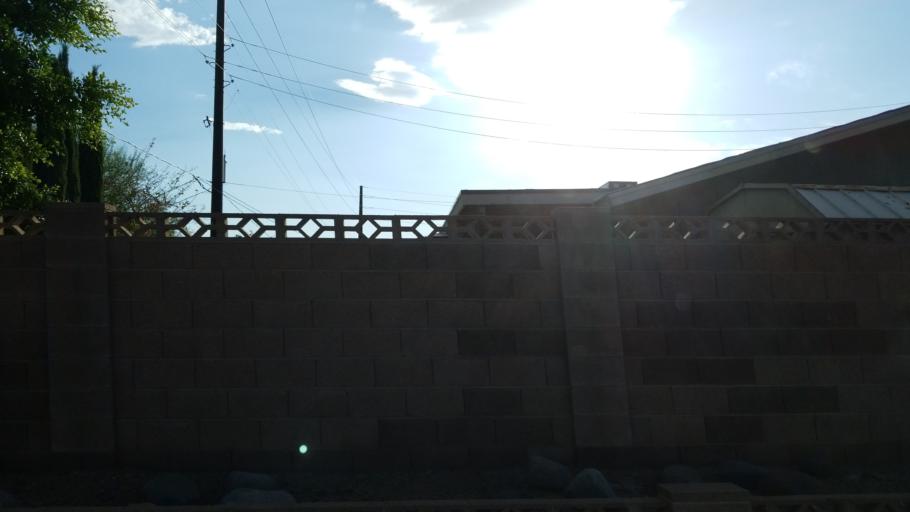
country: US
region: Arizona
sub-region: Maricopa County
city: Scottsdale
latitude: 33.5136
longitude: -111.9046
